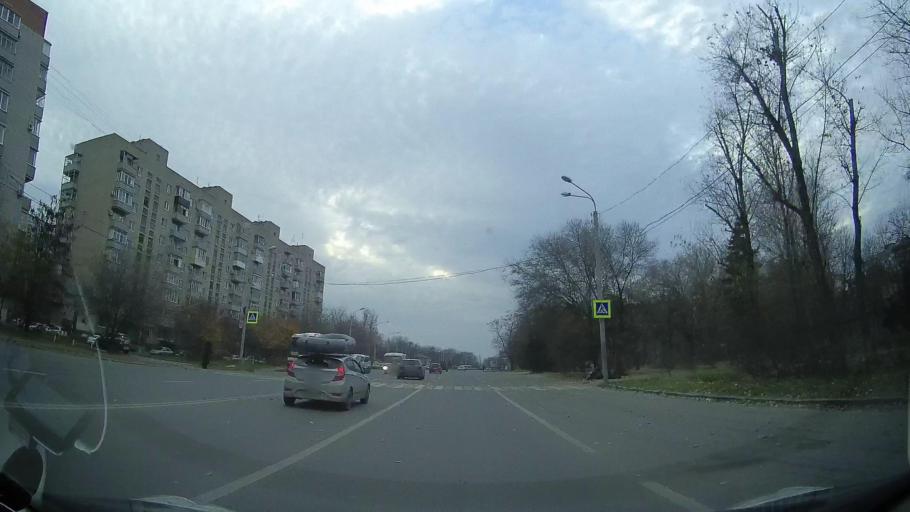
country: RU
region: Rostov
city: Aksay
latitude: 47.2409
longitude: 39.8343
